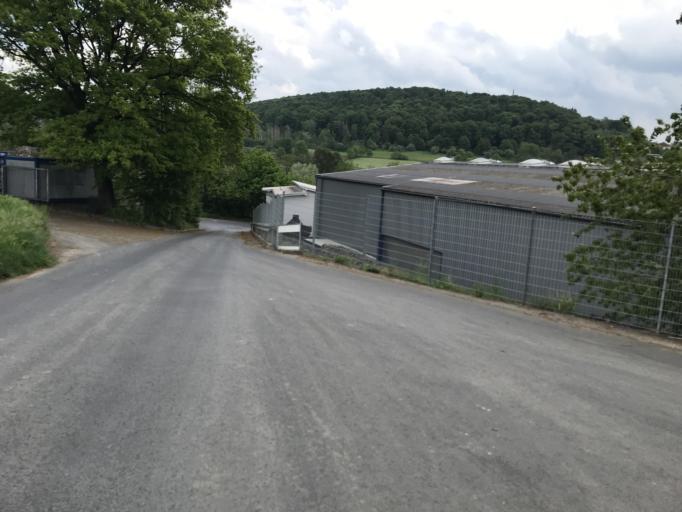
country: DE
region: Hesse
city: Budingen
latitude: 50.3010
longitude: 9.1037
